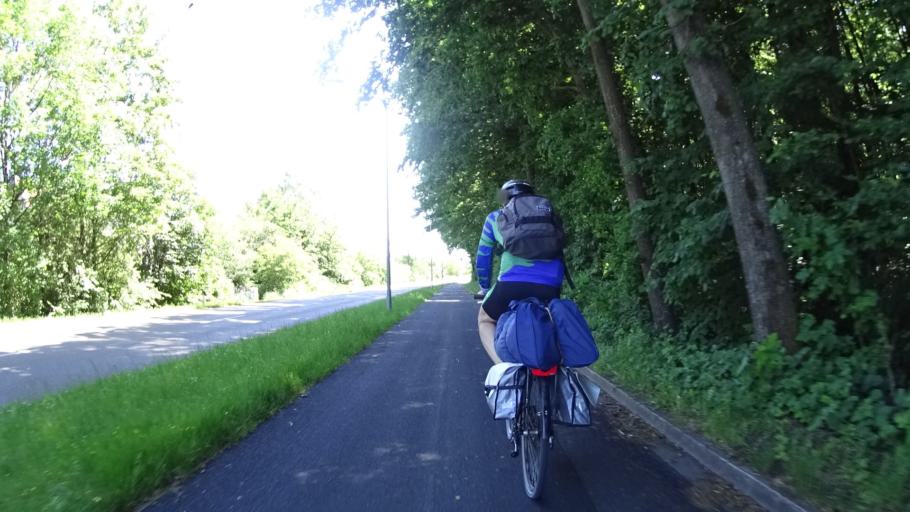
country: DE
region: Bavaria
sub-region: Regierungsbezirk Mittelfranken
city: Gunzenhausen
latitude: 49.1202
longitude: 10.7883
